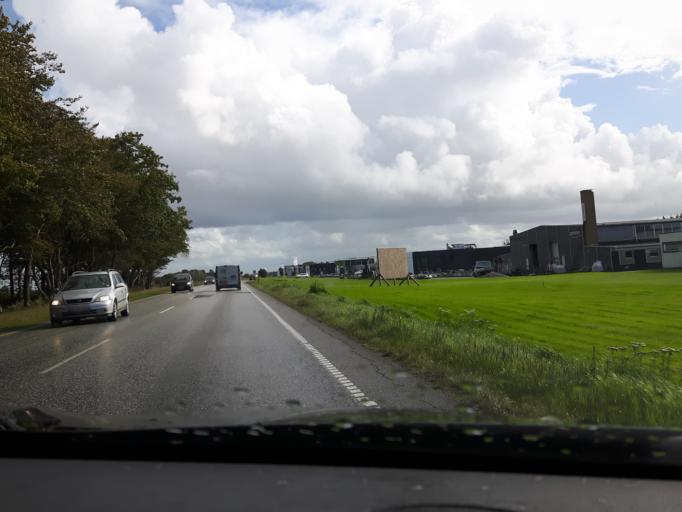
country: DK
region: Central Jutland
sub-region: Holstebro Kommune
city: Holstebro
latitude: 56.3407
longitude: 8.6394
